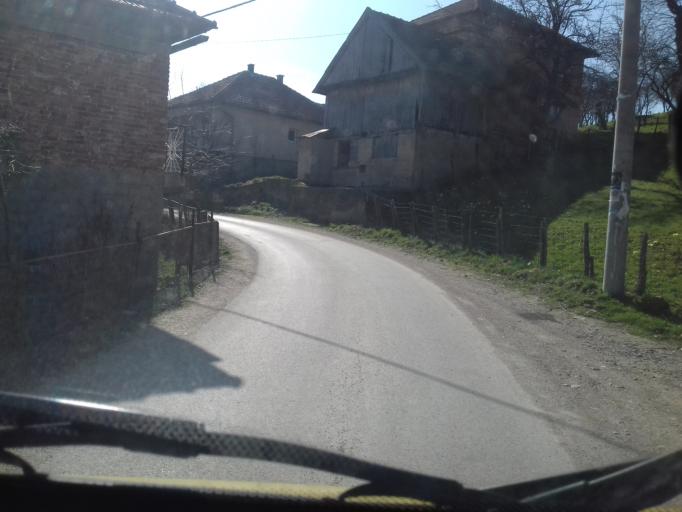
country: BA
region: Federation of Bosnia and Herzegovina
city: Travnik
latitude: 44.2535
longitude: 17.7331
